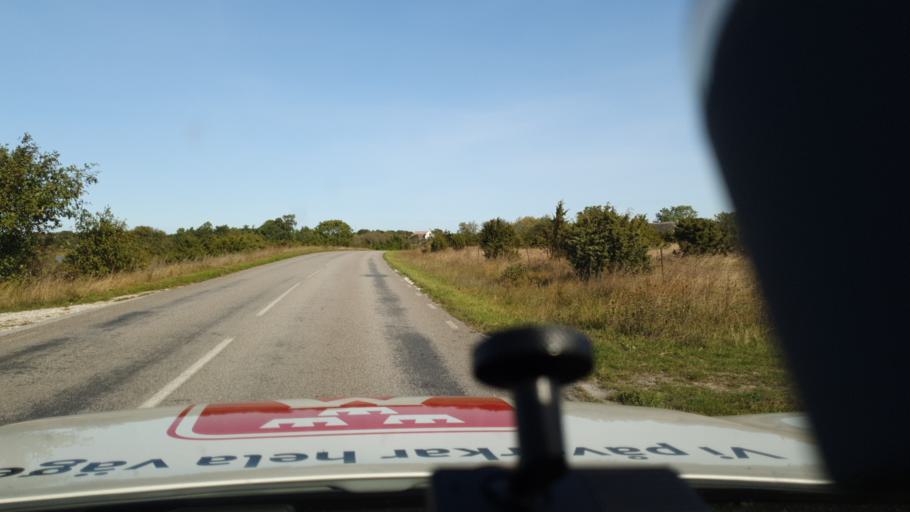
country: SE
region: Gotland
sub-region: Gotland
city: Slite
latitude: 57.9244
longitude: 19.1431
